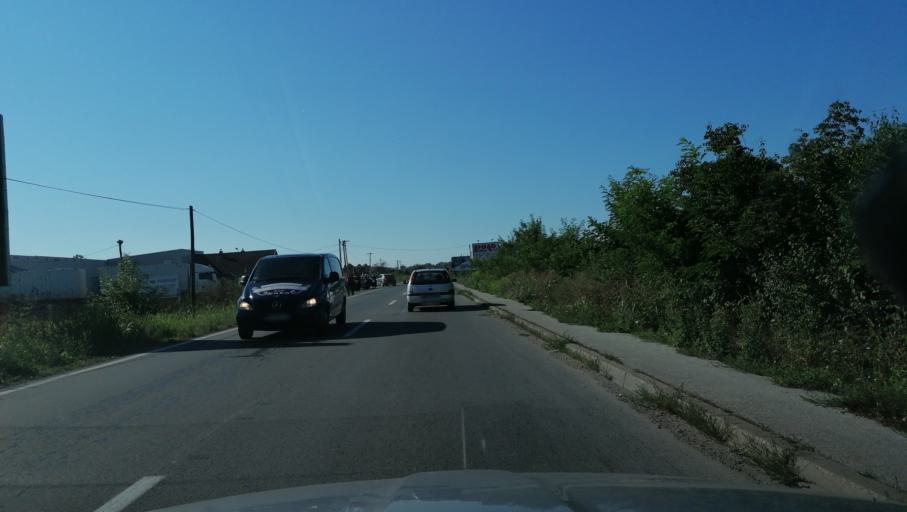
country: RS
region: Central Serbia
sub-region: Raski Okrug
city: Kraljevo
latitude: 43.7591
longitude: 20.6514
